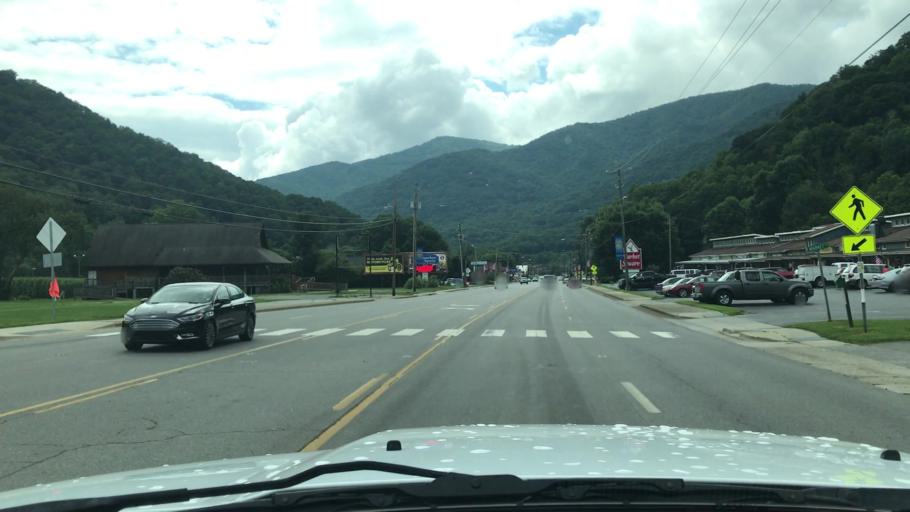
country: US
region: North Carolina
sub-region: Haywood County
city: Maggie Valley
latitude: 35.5167
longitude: -83.0871
